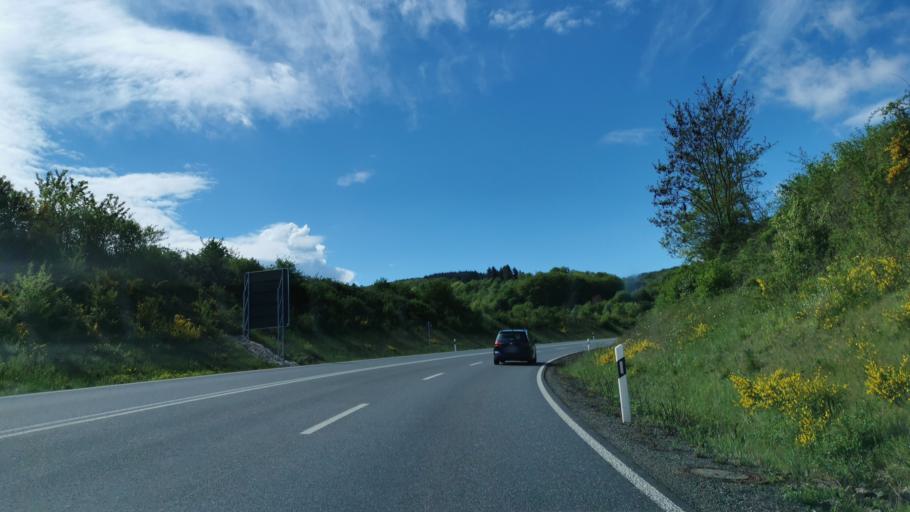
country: DE
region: Rheinland-Pfalz
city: Losnich
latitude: 49.9747
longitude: 7.0366
